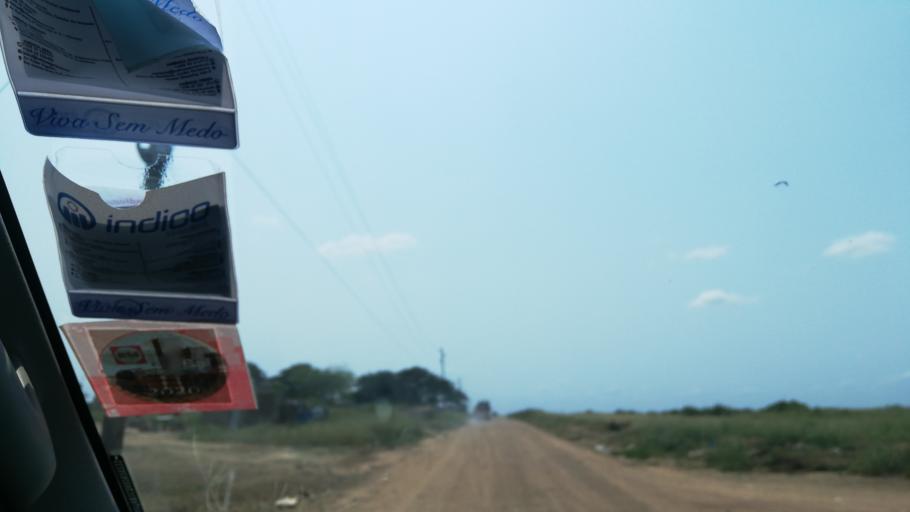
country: MZ
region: Maputo
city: Matola
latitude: -26.0662
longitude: 32.3903
